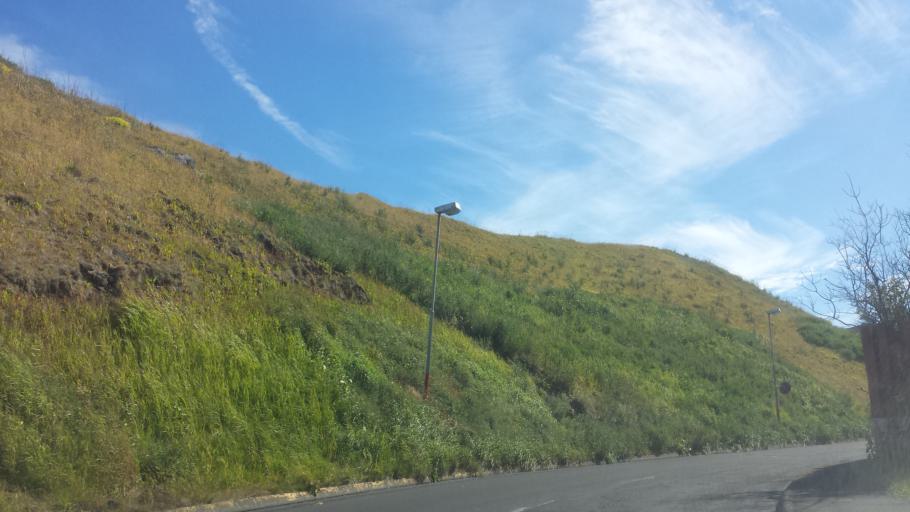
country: IS
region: South
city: Vestmannaeyjar
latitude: 63.4407
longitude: -20.2638
